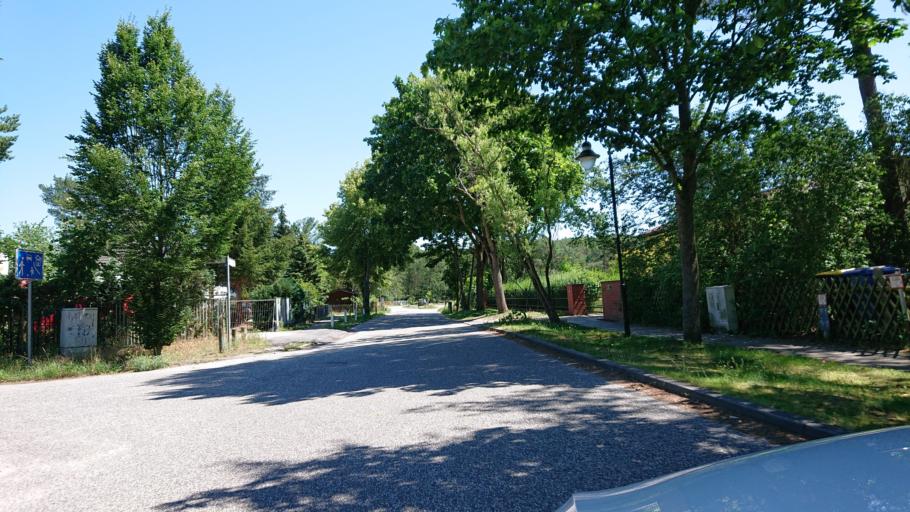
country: DE
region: Brandenburg
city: Potsdam
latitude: 52.3454
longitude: 13.1132
